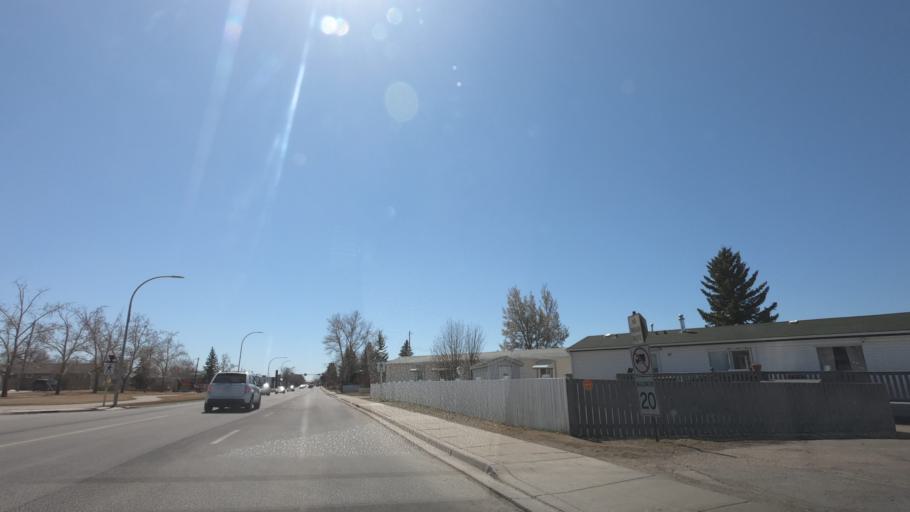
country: CA
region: Alberta
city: Airdrie
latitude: 51.2974
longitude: -114.0135
